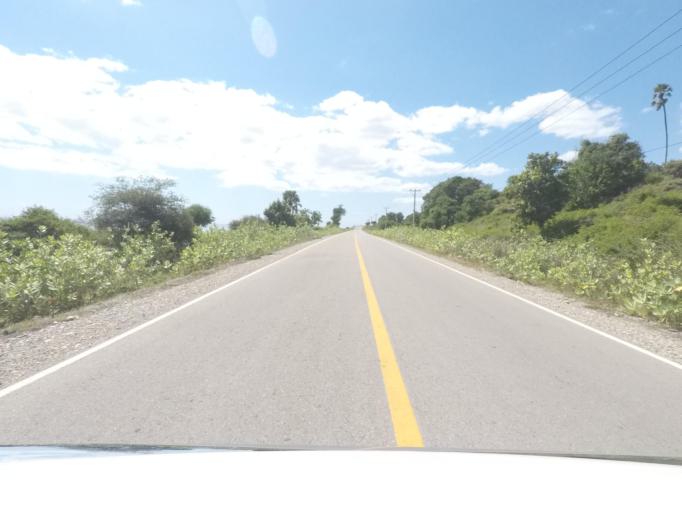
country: TL
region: Lautem
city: Lospalos
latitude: -8.3726
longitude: 126.8770
